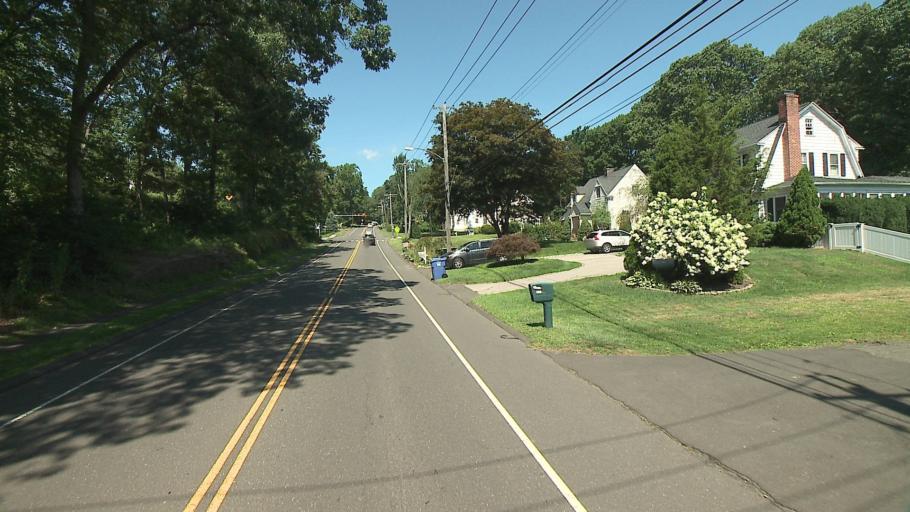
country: US
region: Connecticut
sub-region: Fairfield County
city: Trumbull
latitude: 41.2507
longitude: -73.2099
